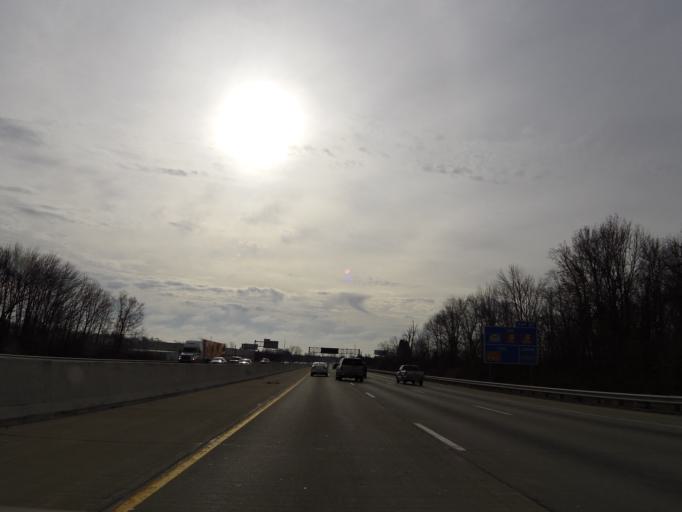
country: US
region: Indiana
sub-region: Marion County
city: Warren Park
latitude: 39.7658
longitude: -86.0296
